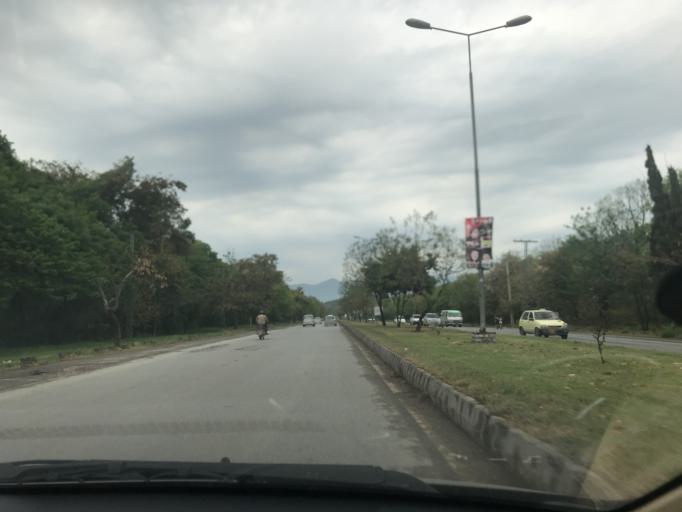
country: PK
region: Islamabad
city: Islamabad
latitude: 33.6806
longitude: 73.1387
